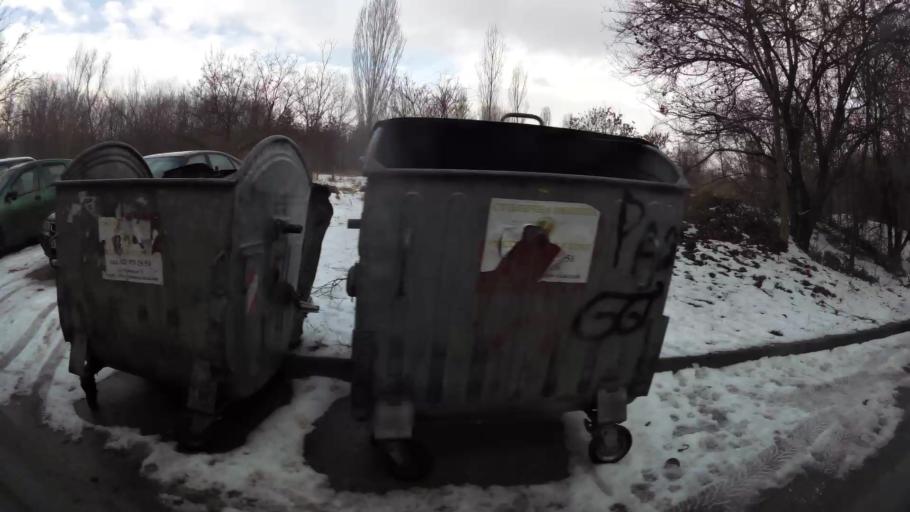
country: BG
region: Sofia-Capital
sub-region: Stolichna Obshtina
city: Sofia
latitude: 42.7069
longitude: 23.2752
